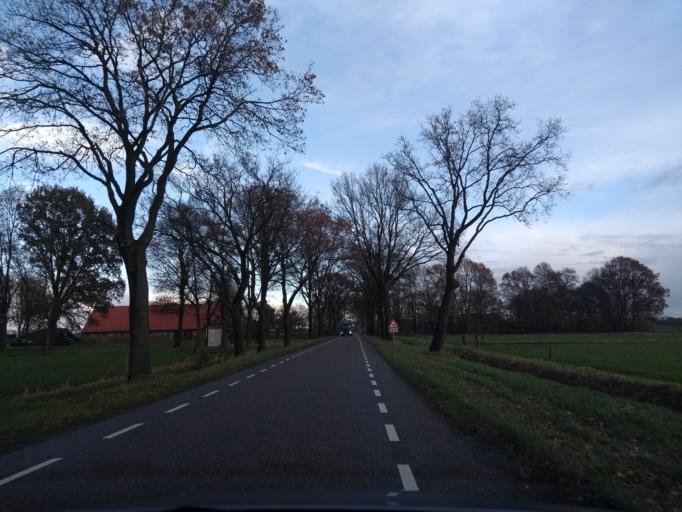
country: NL
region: Overijssel
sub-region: Gemeente Twenterand
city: Vriezenveen
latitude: 52.4046
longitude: 6.6699
